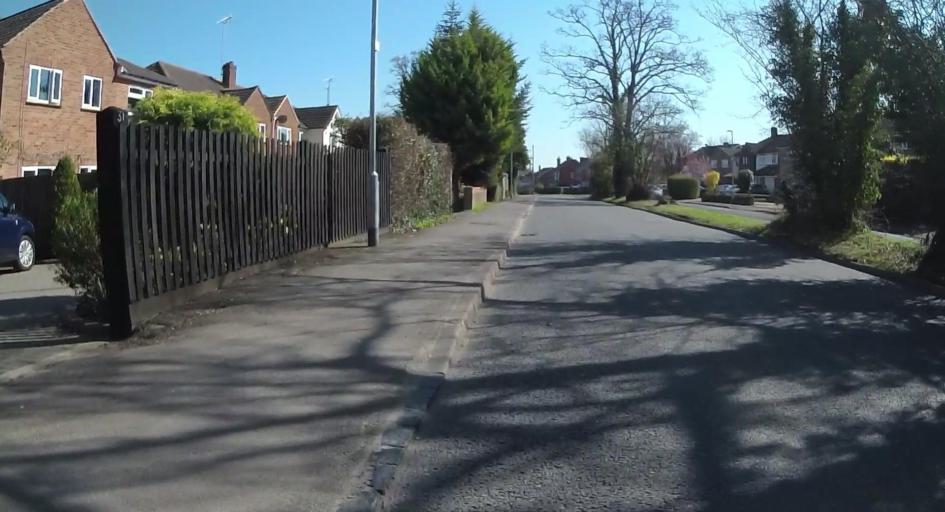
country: GB
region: England
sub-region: Wokingham
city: Winnersh
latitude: 51.4242
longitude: -0.8563
